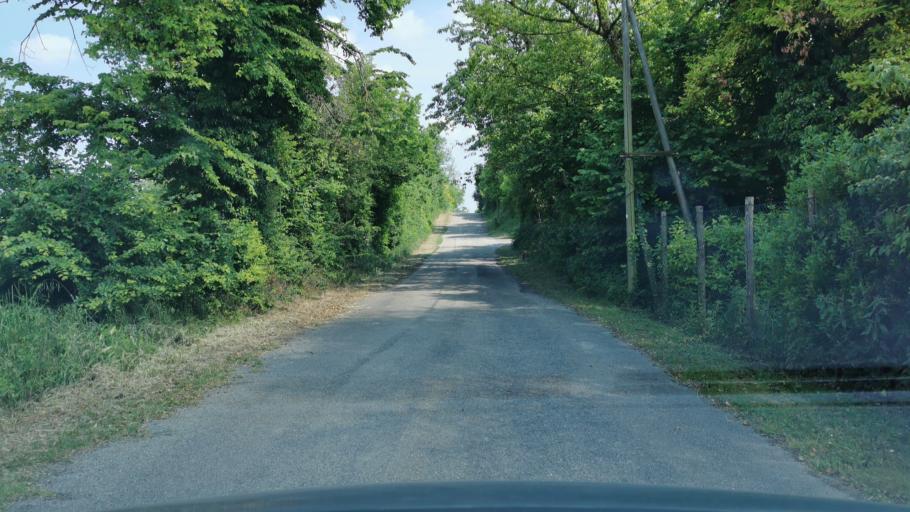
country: IT
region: Piedmont
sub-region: Provincia di Asti
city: Grazzano Badoglio
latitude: 45.0556
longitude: 8.3129
